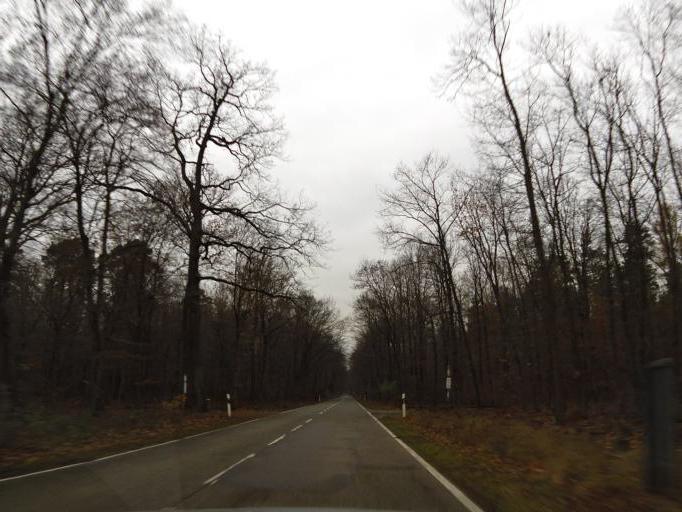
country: DE
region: Hesse
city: Kelsterbach
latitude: 50.0648
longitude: 8.5712
